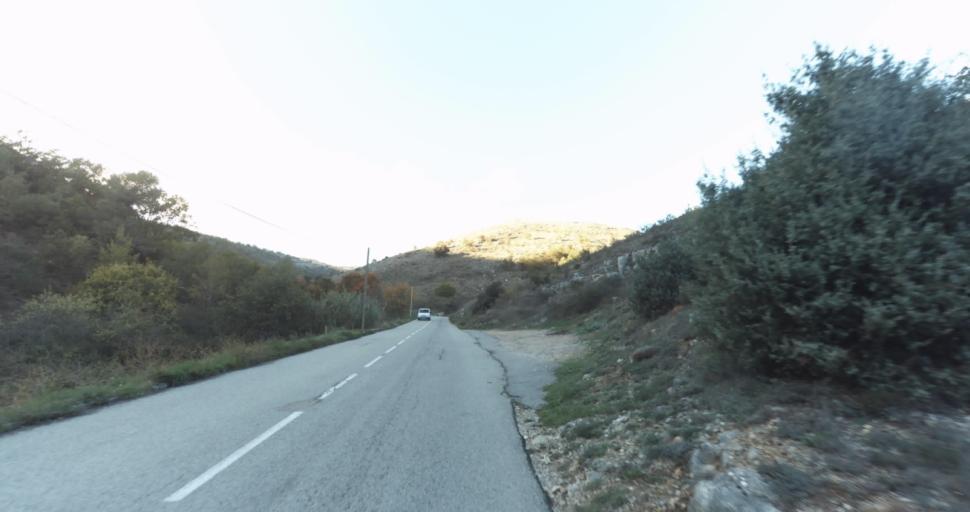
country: FR
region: Provence-Alpes-Cote d'Azur
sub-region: Departement des Alpes-Maritimes
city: Vence
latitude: 43.7455
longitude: 7.1019
